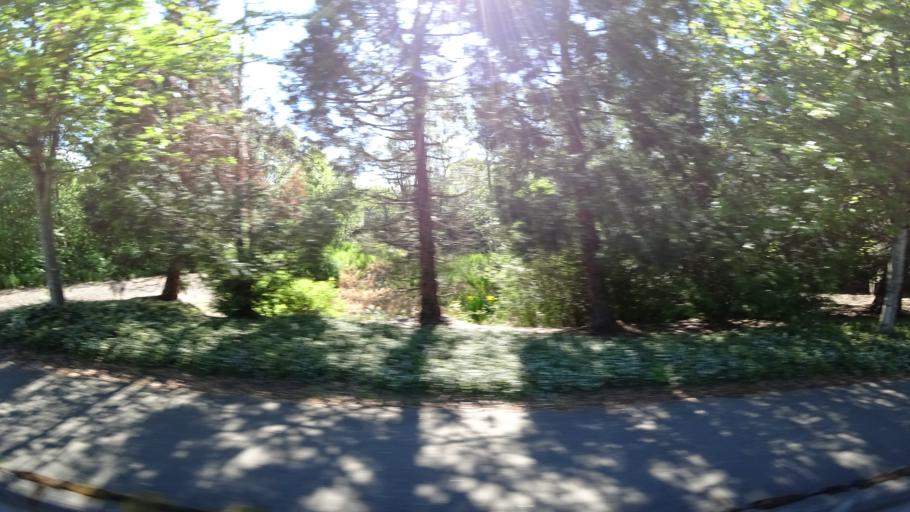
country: US
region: Oregon
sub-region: Washington County
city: Oak Hills
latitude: 45.5473
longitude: -122.8301
